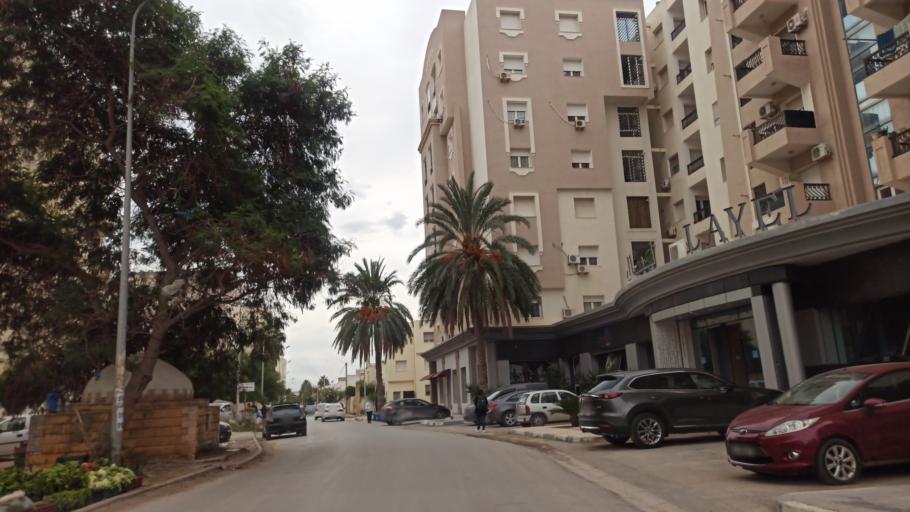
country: TN
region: Tunis
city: La Goulette
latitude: 36.8569
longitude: 10.2671
